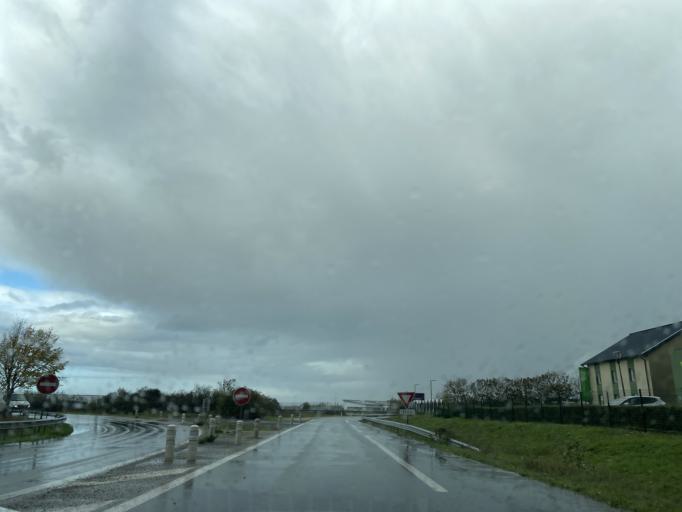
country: FR
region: Centre
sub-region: Departement du Cher
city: La Chapelle-Saint-Ursin
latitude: 47.0488
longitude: 2.3444
